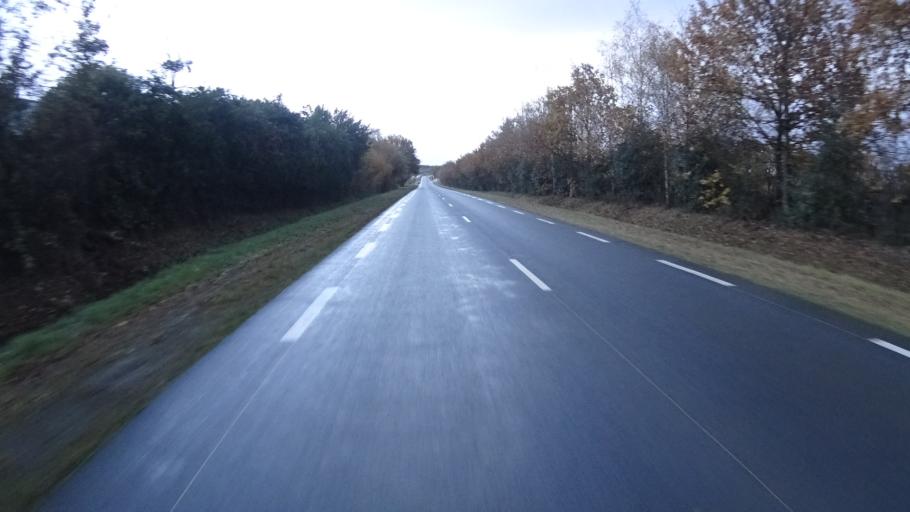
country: FR
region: Brittany
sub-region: Departement d'Ille-et-Vilaine
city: Bains-sur-Oust
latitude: 47.6917
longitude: -2.0469
